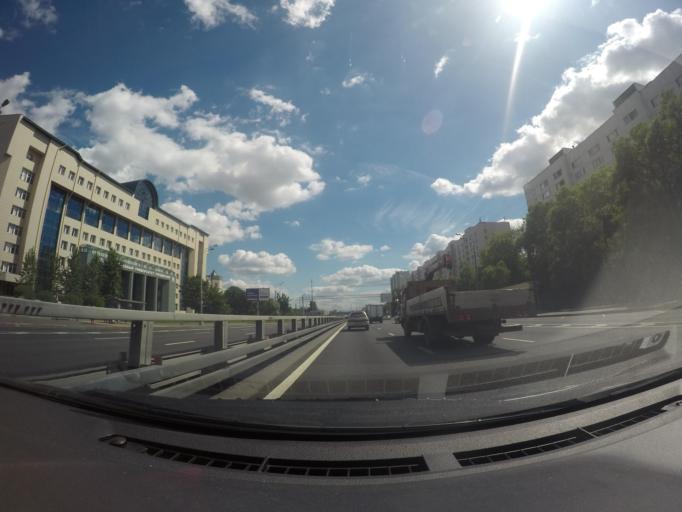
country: RU
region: Moscow
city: Vykhino-Zhulebino
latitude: 55.7138
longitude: 37.8101
